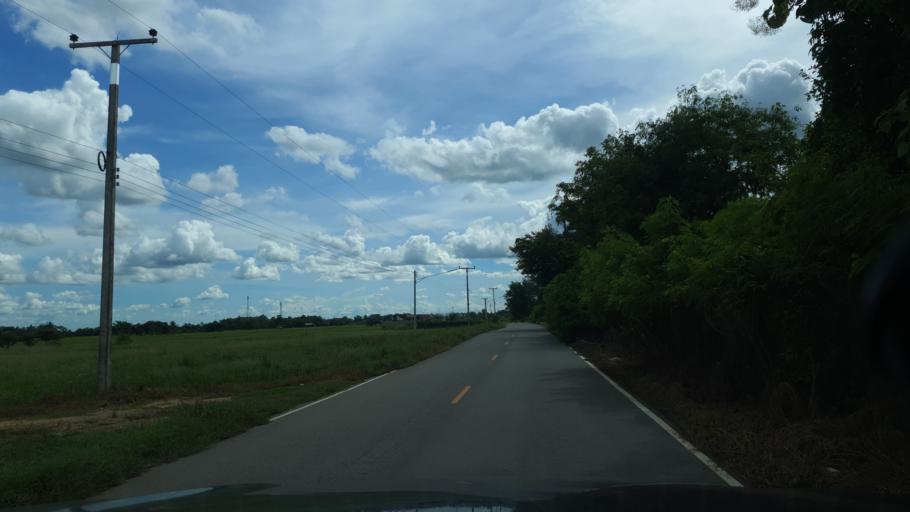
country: TH
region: Sukhothai
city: Thung Saliam
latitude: 17.3410
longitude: 99.6359
